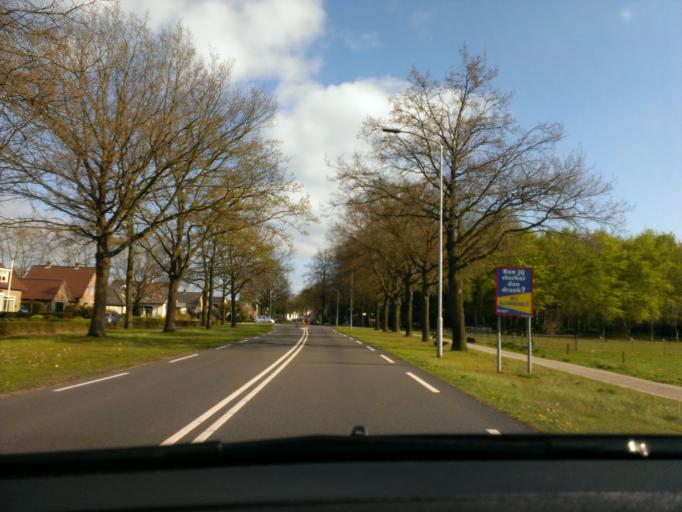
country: NL
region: Gelderland
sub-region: Gemeente Heerde
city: Heerde
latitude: 52.3935
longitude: 6.0341
